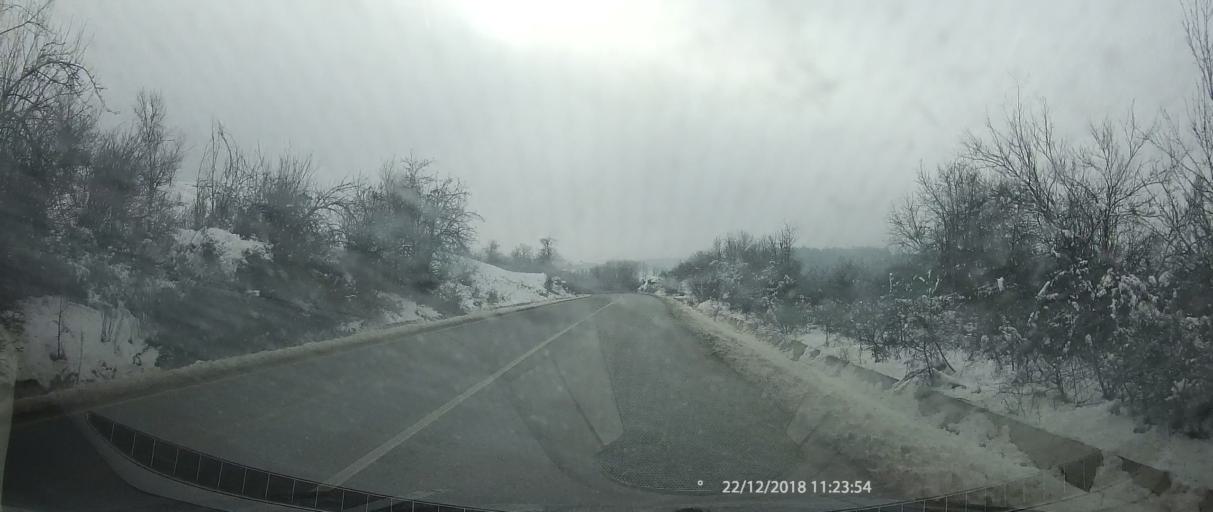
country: BG
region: Kyustendil
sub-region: Obshtina Boboshevo
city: Boboshevo
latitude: 42.2549
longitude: 22.8859
